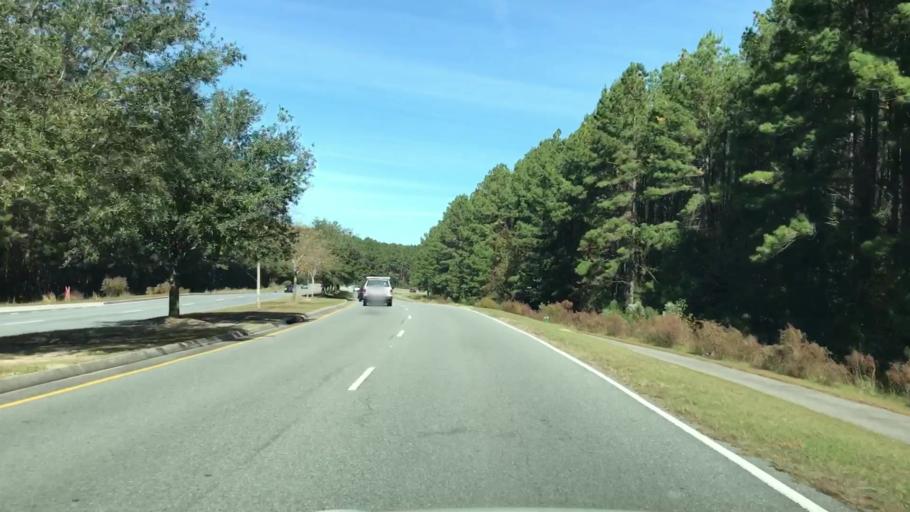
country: US
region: South Carolina
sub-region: Beaufort County
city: Bluffton
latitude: 32.2760
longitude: -80.9133
